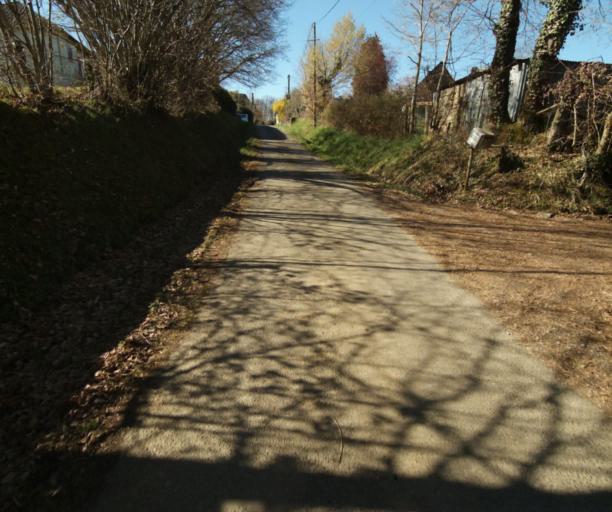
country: FR
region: Limousin
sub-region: Departement de la Correze
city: Chamboulive
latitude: 45.4130
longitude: 1.6991
